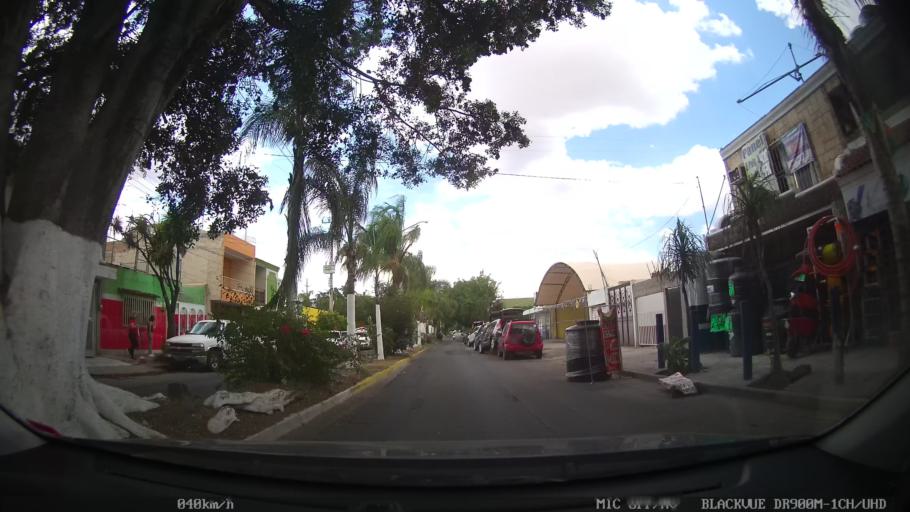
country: MX
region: Jalisco
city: Tlaquepaque
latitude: 20.6565
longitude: -103.2821
